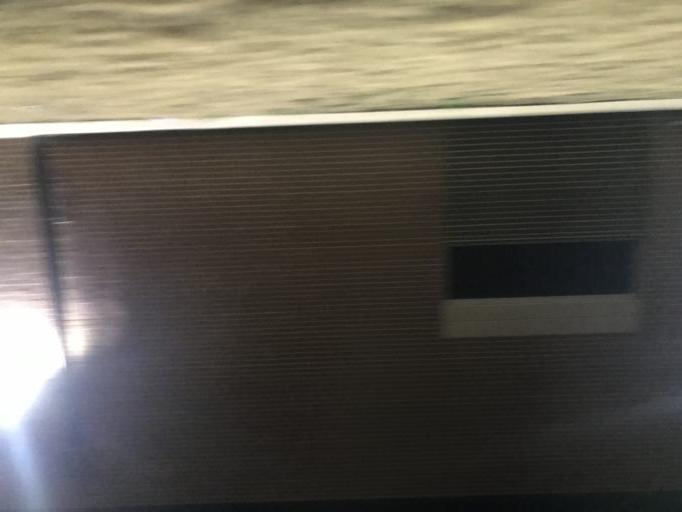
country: US
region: Texas
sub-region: Taylor County
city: Potosi
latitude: 32.3749
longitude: -99.7153
